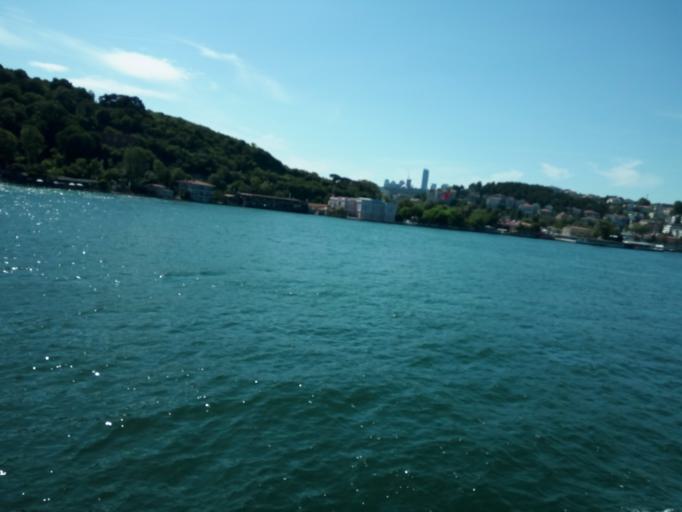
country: TR
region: Istanbul
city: Sisli
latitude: 41.0939
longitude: 29.0579
